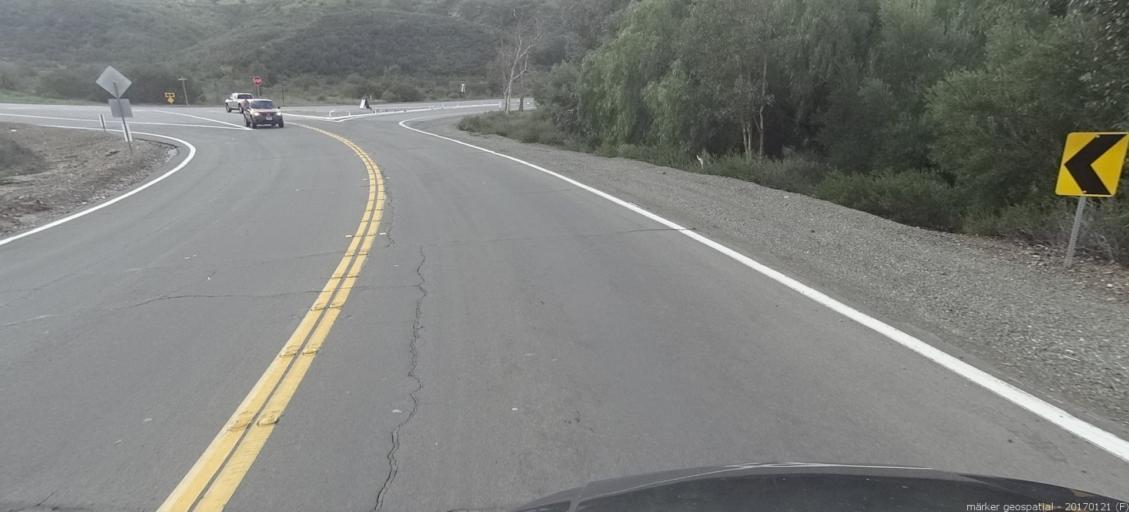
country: US
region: California
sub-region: Orange County
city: Foothill Ranch
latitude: 33.7490
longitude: -117.6730
